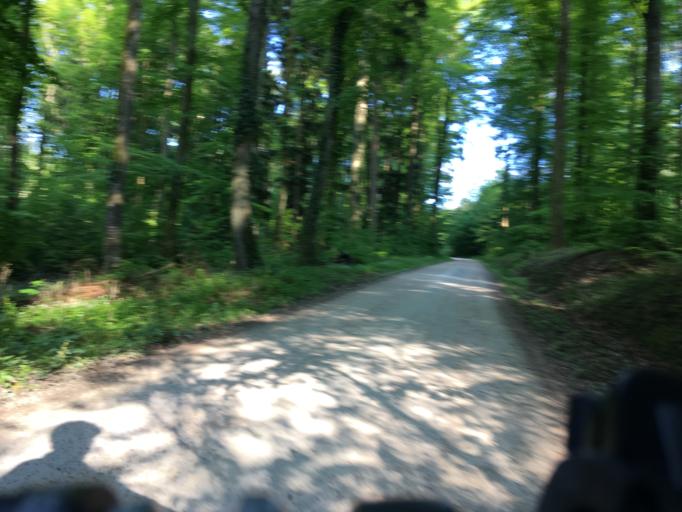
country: DE
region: Baden-Wuerttemberg
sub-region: Freiburg Region
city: Gailingen
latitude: 47.7087
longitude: 8.7475
